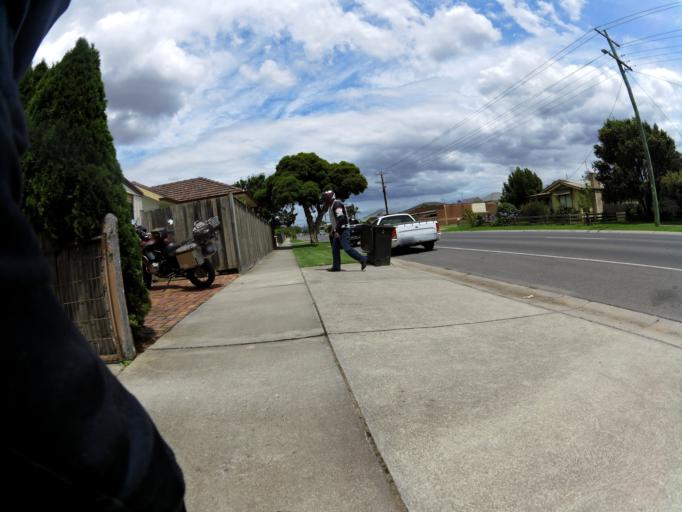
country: AU
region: Victoria
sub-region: Latrobe
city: Traralgon
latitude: -38.1895
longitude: 146.5343
